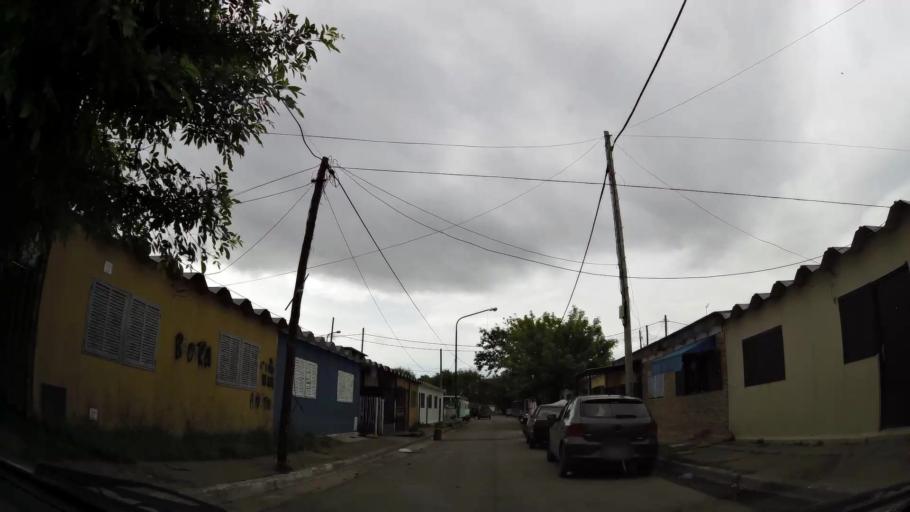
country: AR
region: Buenos Aires
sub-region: Partido de Quilmes
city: Quilmes
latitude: -34.7542
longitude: -58.2510
